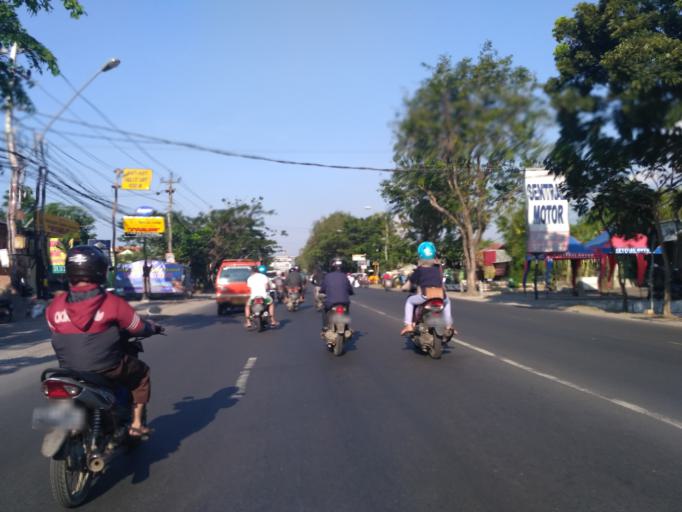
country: ID
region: Central Java
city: Semarang
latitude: -7.0093
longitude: 110.4668
